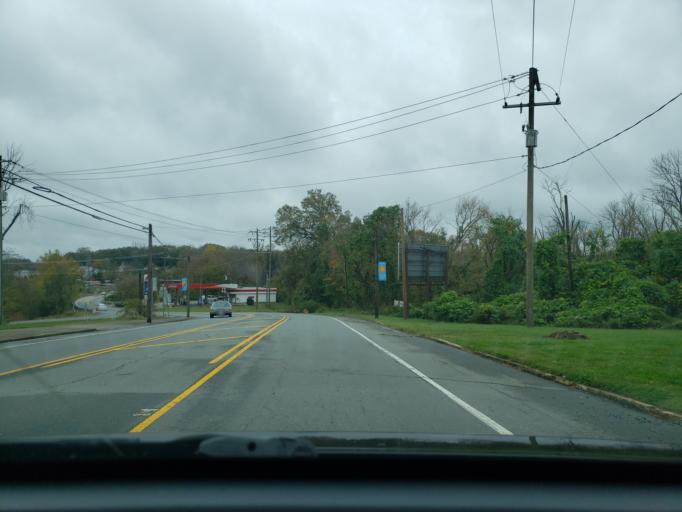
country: US
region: North Carolina
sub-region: Stokes County
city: Walnut Cove
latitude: 36.2937
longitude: -80.1418
